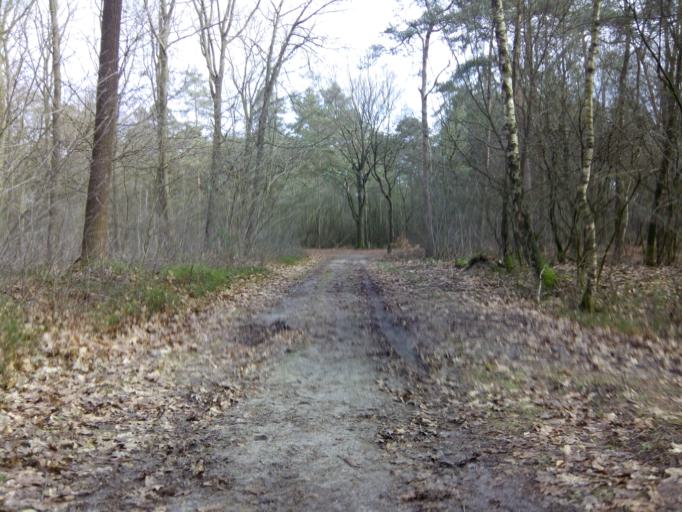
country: NL
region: Utrecht
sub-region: Gemeente Utrechtse Heuvelrug
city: Driebergen-Rijsenburg
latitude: 52.1073
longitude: 5.3002
